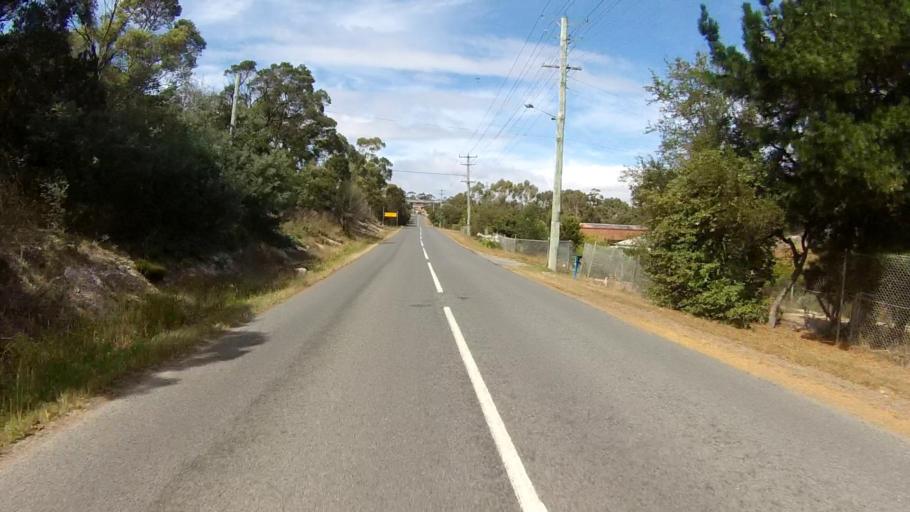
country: AU
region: Tasmania
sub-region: Clarence
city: Lindisfarne
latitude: -42.8175
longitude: 147.3513
